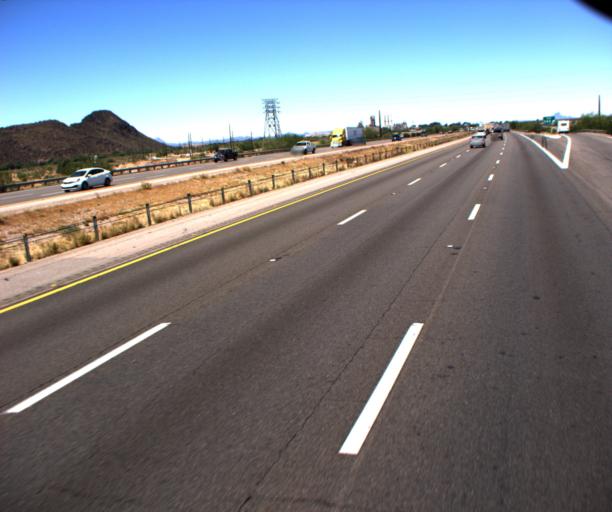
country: US
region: Arizona
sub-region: Pima County
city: Marana
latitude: 32.3982
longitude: -111.1269
